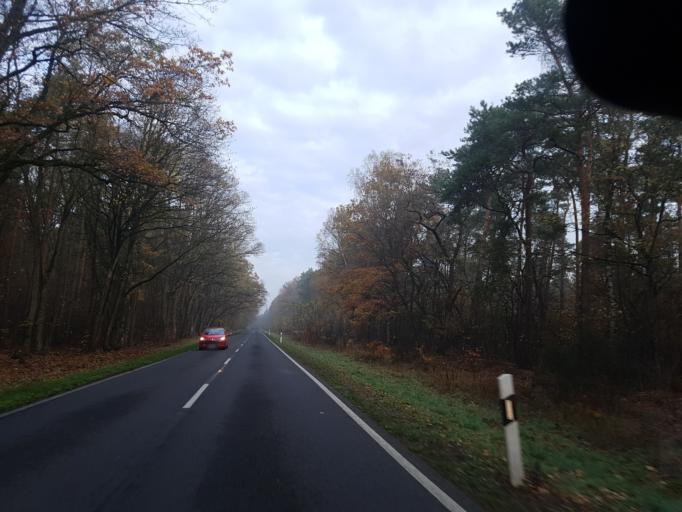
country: DE
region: Saxony-Anhalt
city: Kropstadt
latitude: 51.9450
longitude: 12.7540
